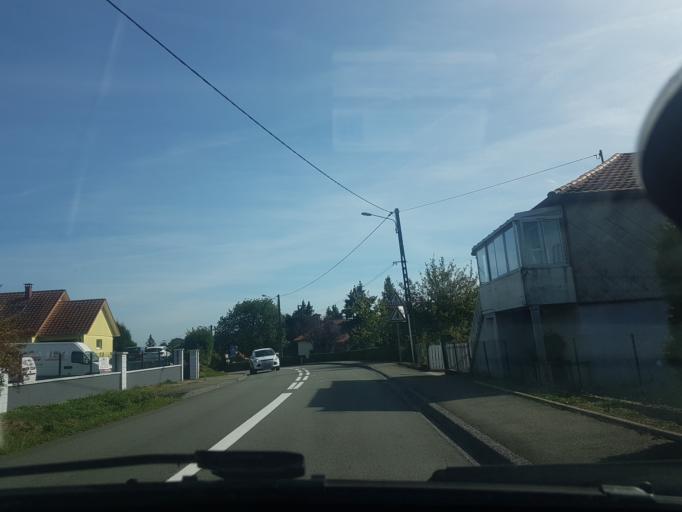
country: FR
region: Franche-Comte
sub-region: Territoire de Belfort
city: Offemont
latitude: 47.6682
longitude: 6.9115
